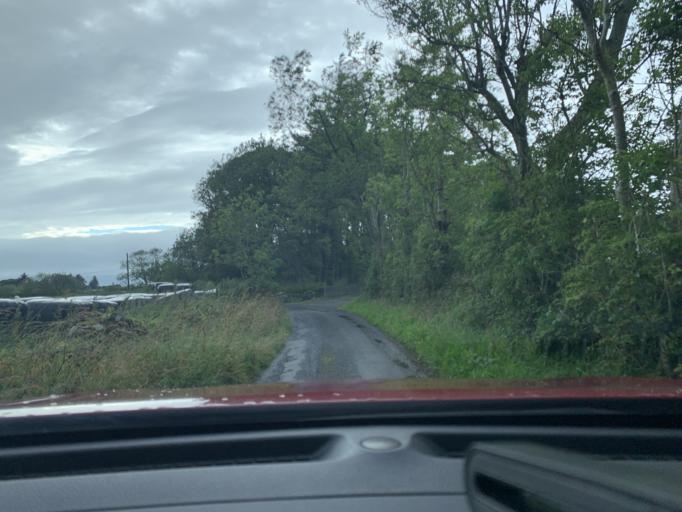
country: IE
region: Connaught
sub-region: Sligo
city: Strandhill
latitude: 54.3619
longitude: -8.5538
